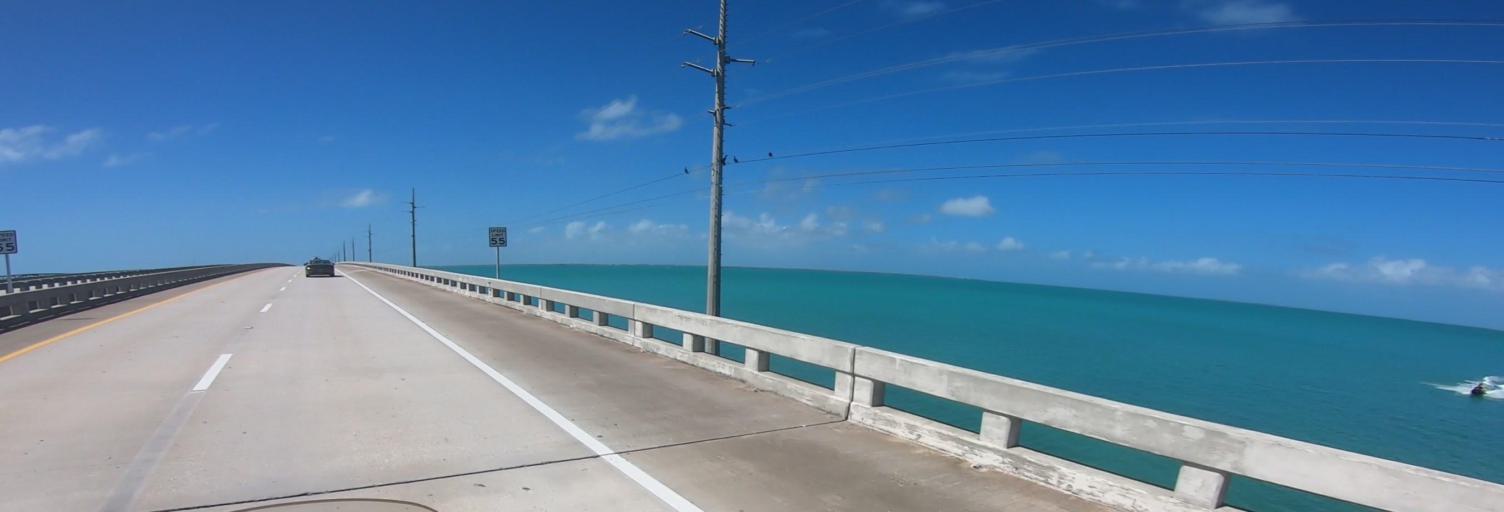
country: US
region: Florida
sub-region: Monroe County
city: Big Pine Key
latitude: 24.6600
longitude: -81.2790
